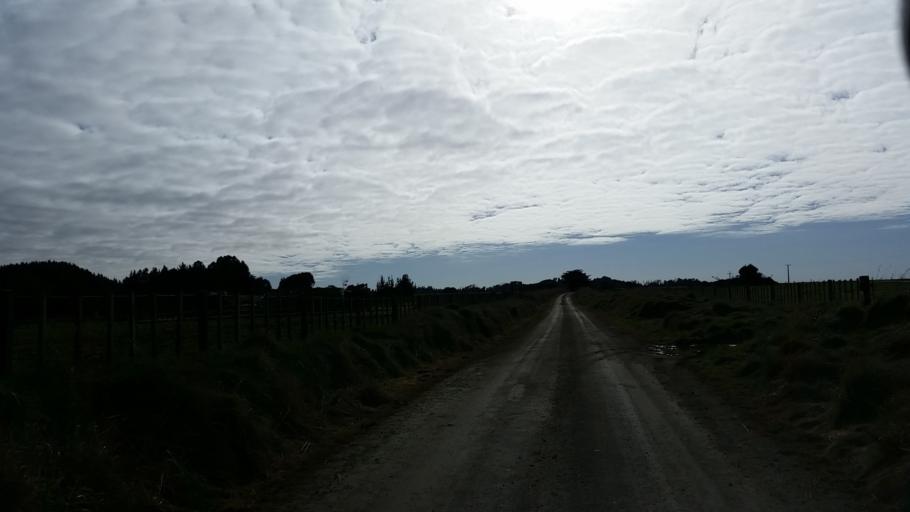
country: NZ
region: Taranaki
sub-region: South Taranaki District
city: Patea
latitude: -39.6806
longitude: 174.6605
